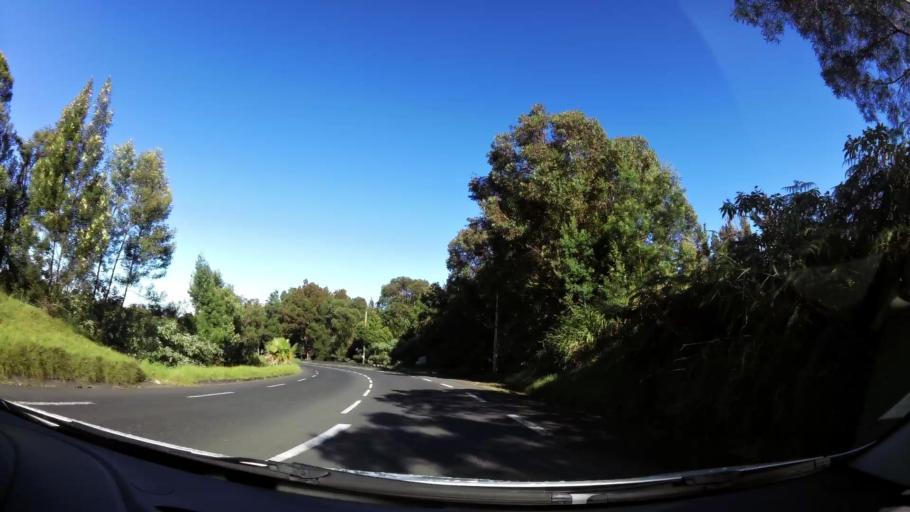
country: RE
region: Reunion
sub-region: Reunion
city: Le Tampon
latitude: -21.2143
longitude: 55.5641
